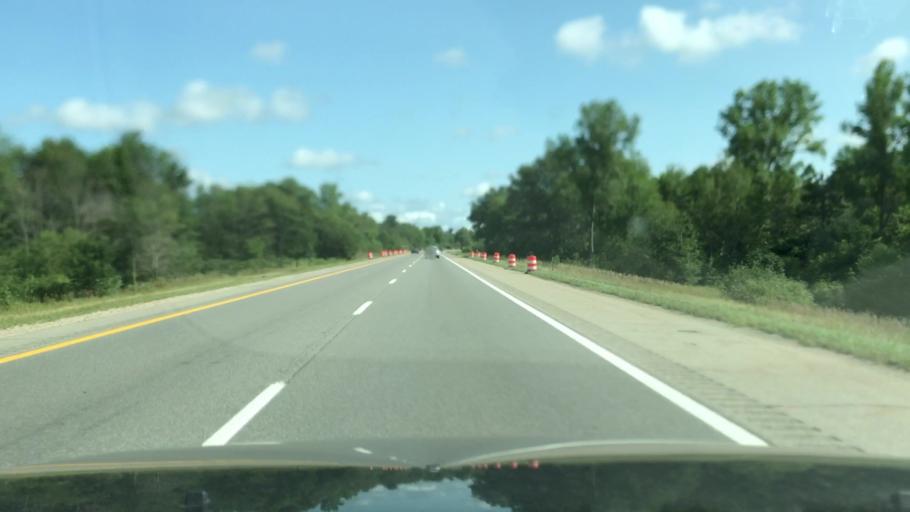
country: US
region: Michigan
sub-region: Kent County
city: Cedar Springs
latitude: 43.2460
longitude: -85.5595
